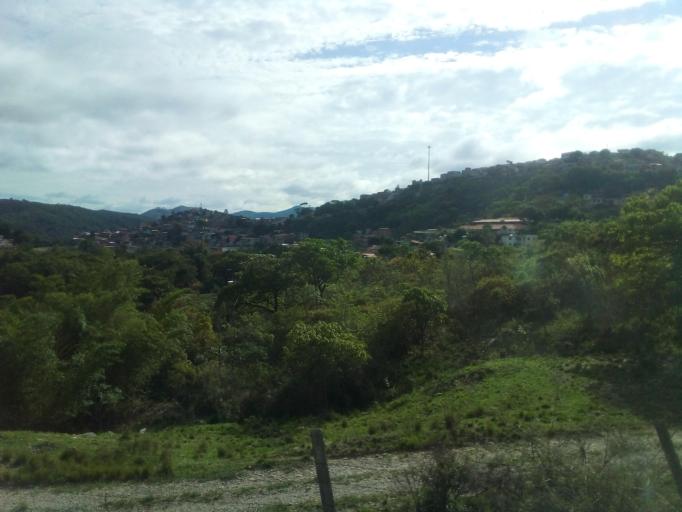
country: BR
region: Minas Gerais
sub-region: Belo Horizonte
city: Belo Horizonte
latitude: -19.8873
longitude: -43.8636
